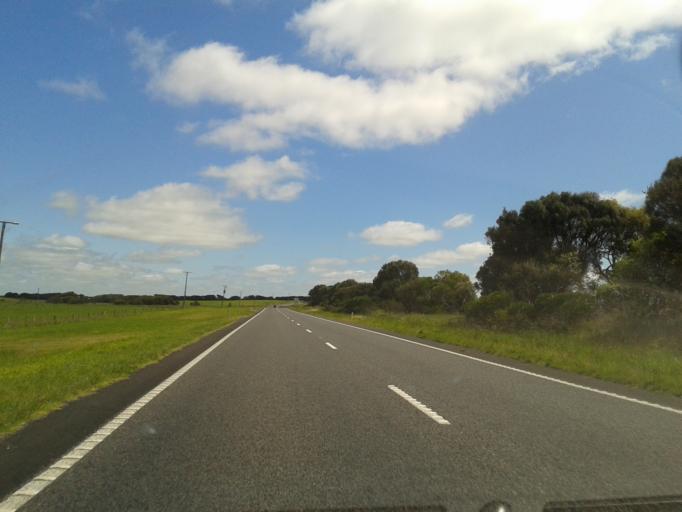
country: AU
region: Victoria
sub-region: Moyne
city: Port Fairy
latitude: -38.2965
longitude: 142.0229
